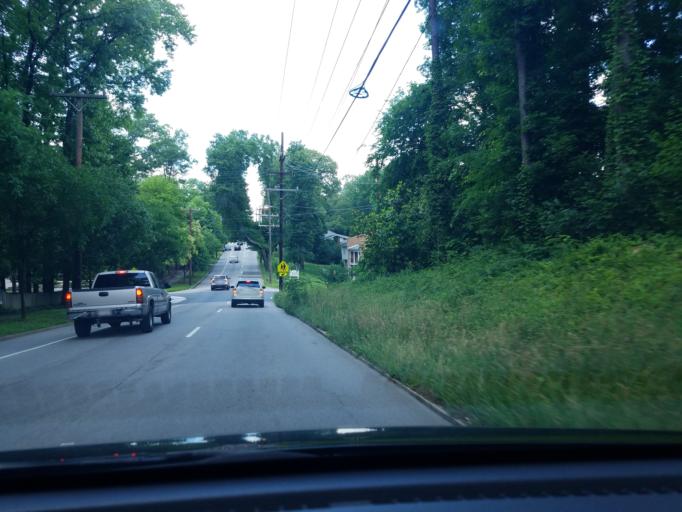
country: US
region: North Carolina
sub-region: Durham County
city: Durham
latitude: 36.0082
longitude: -78.9056
